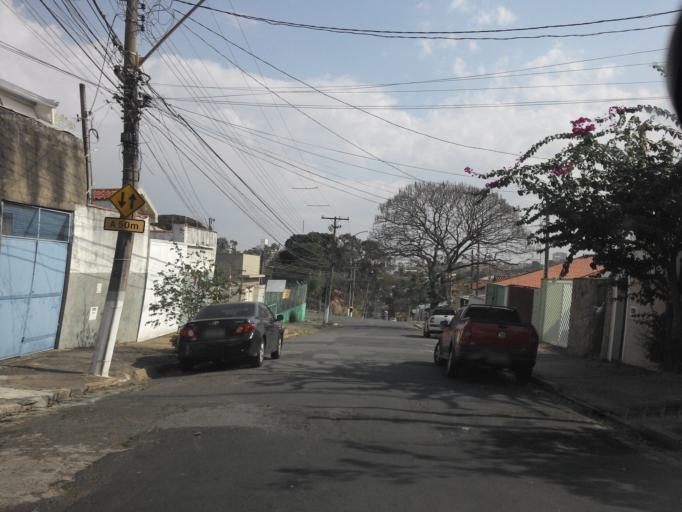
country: BR
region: Sao Paulo
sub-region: Campinas
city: Campinas
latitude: -22.9116
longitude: -47.0669
